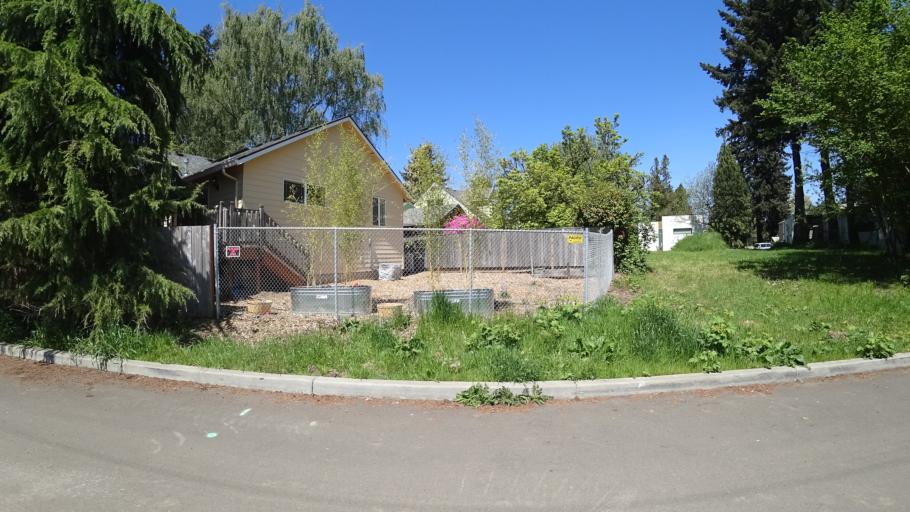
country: US
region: Oregon
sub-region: Clackamas County
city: Milwaukie
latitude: 45.4634
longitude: -122.6221
